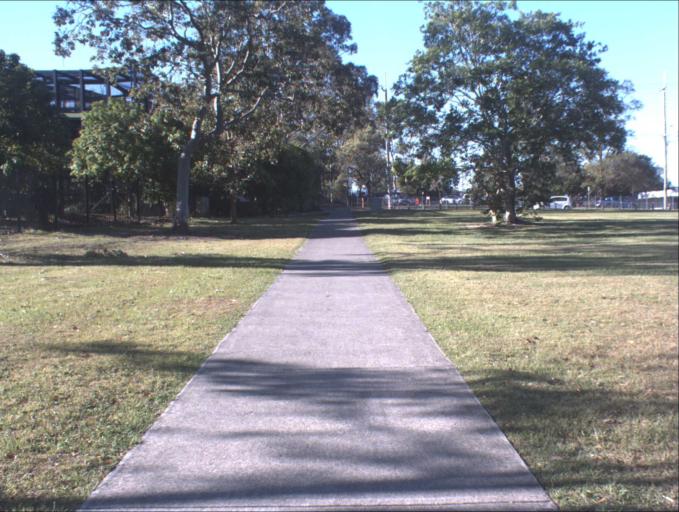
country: AU
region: Queensland
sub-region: Logan
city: Logan City
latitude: -27.6407
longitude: 153.1288
